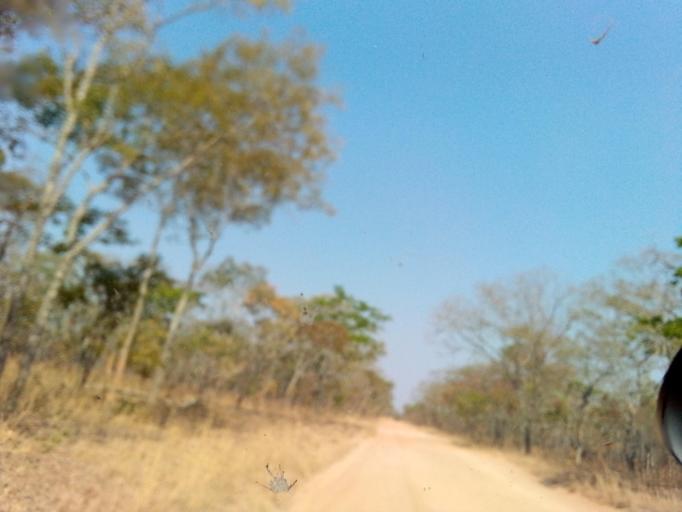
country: ZM
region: Northern
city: Mpika
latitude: -12.2419
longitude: 30.8294
